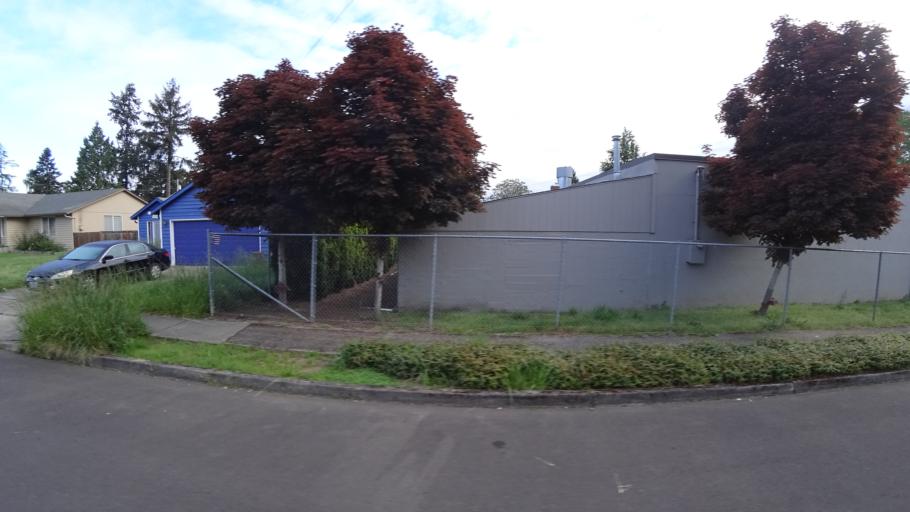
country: US
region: Oregon
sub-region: Washington County
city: Beaverton
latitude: 45.4827
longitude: -122.8126
